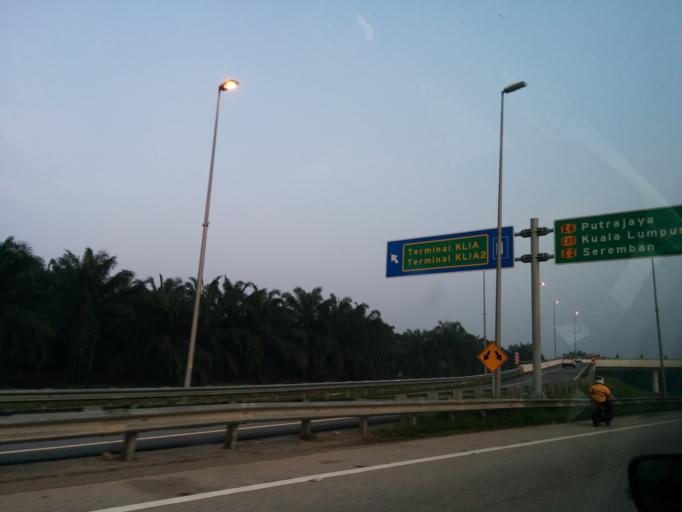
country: MY
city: Sungai Pelek New Village
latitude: 2.7599
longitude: 101.6868
